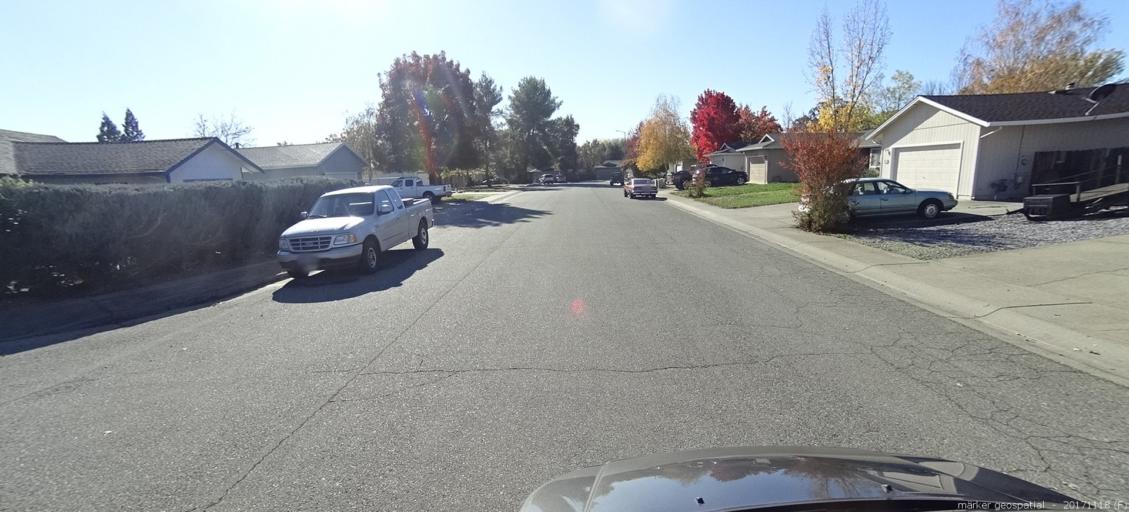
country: US
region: California
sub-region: Shasta County
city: Cottonwood
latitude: 40.3852
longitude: -122.2905
